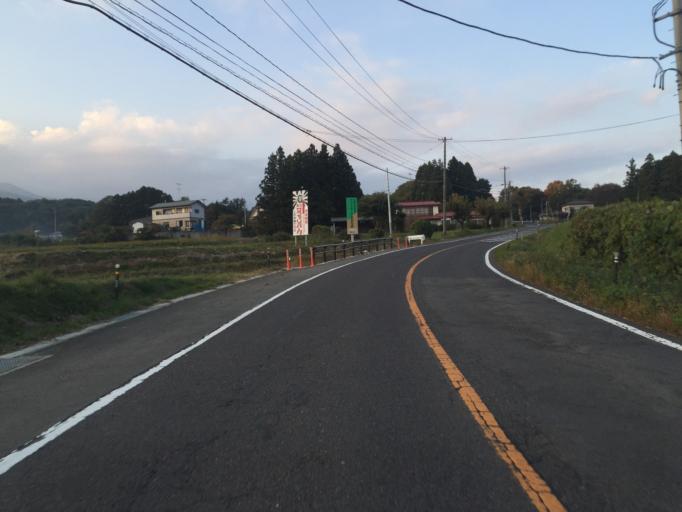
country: JP
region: Fukushima
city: Motomiya
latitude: 37.5681
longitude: 140.3508
